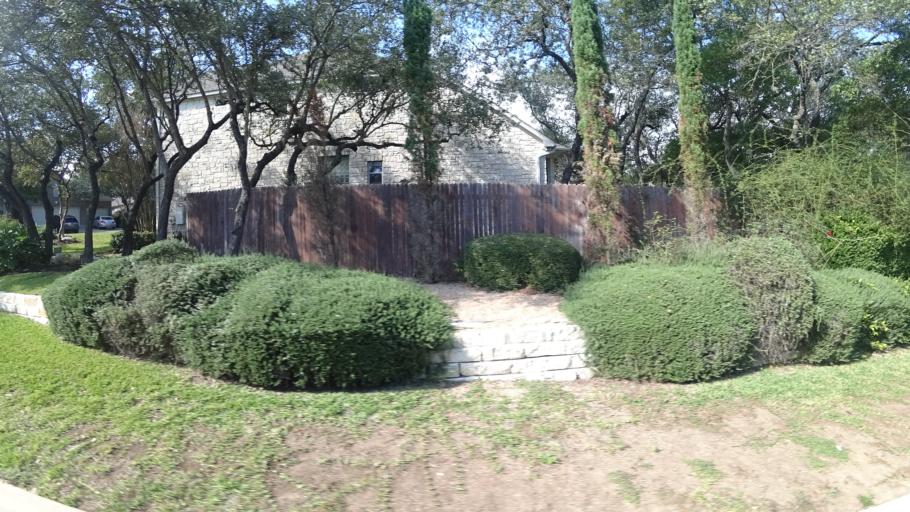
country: US
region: Texas
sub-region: Travis County
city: Hudson Bend
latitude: 30.3796
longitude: -97.9022
